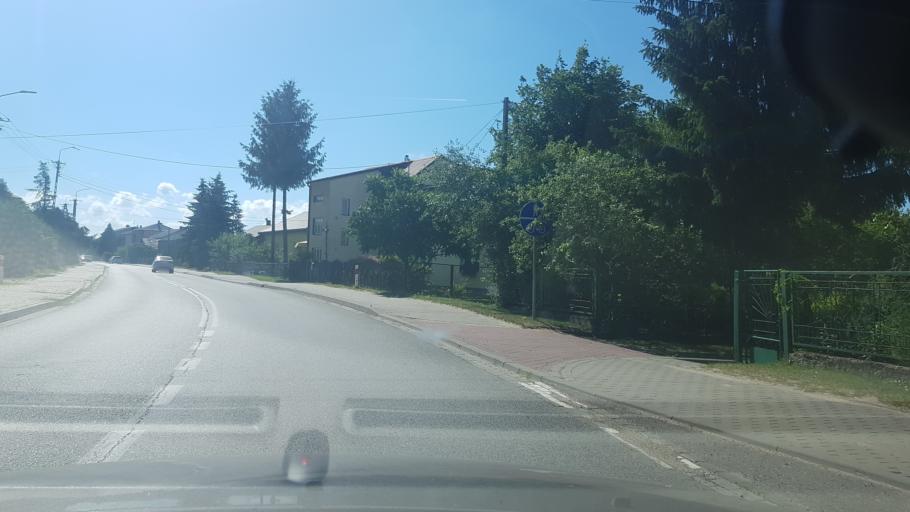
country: PL
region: Masovian Voivodeship
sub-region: Powiat siedlecki
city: Suchozebry
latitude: 52.2132
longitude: 22.2290
